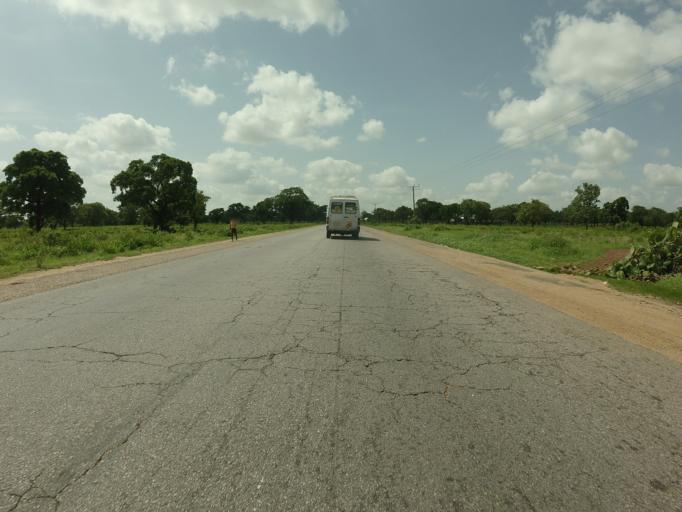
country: GH
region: Northern
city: Savelugu
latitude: 9.5727
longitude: -0.8348
